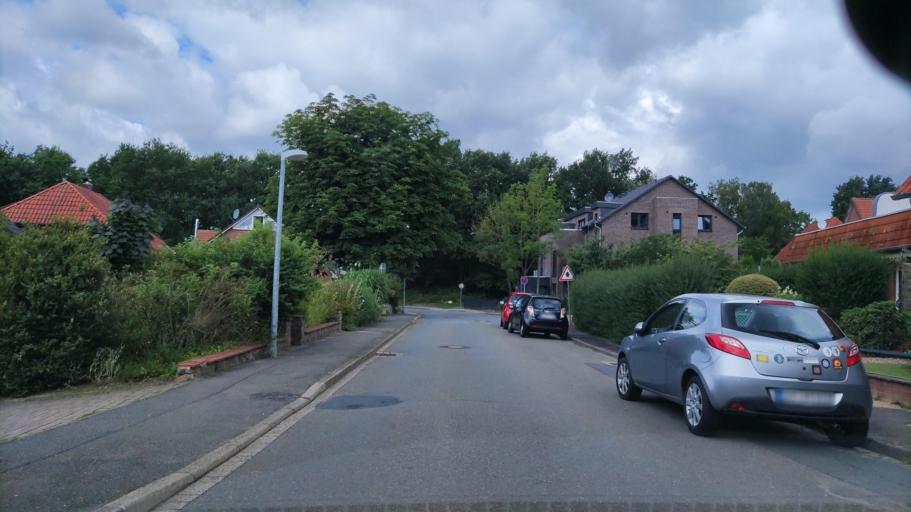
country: DE
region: Lower Saxony
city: Lueneburg
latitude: 53.2268
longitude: 10.3873
